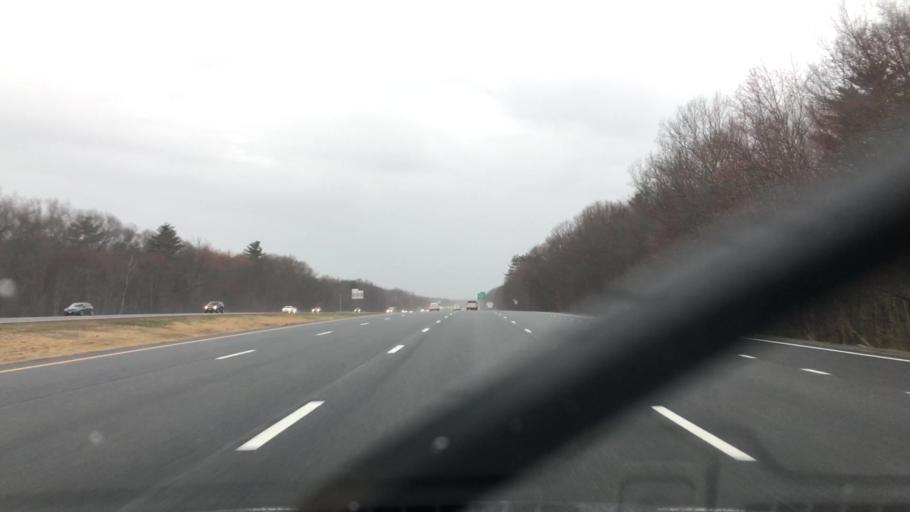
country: US
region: Massachusetts
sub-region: Essex County
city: Newburyport
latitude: 42.7750
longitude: -70.9300
